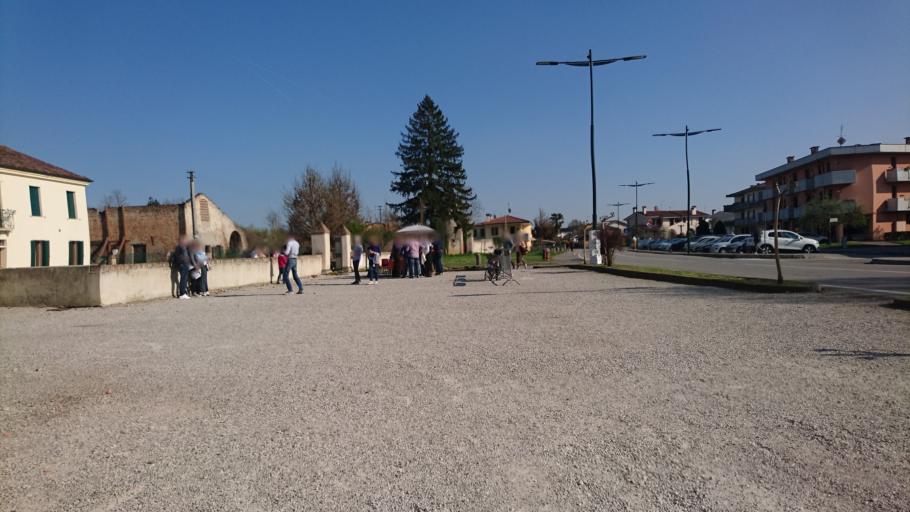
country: IT
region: Veneto
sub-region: Provincia di Padova
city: Vigonza
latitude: 45.4435
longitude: 11.9908
